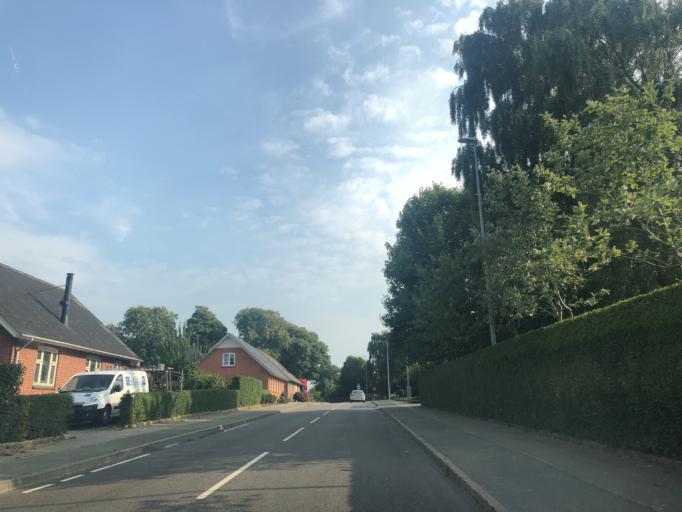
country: DK
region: Central Jutland
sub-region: Skive Kommune
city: Skive
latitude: 56.6513
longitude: 8.9328
